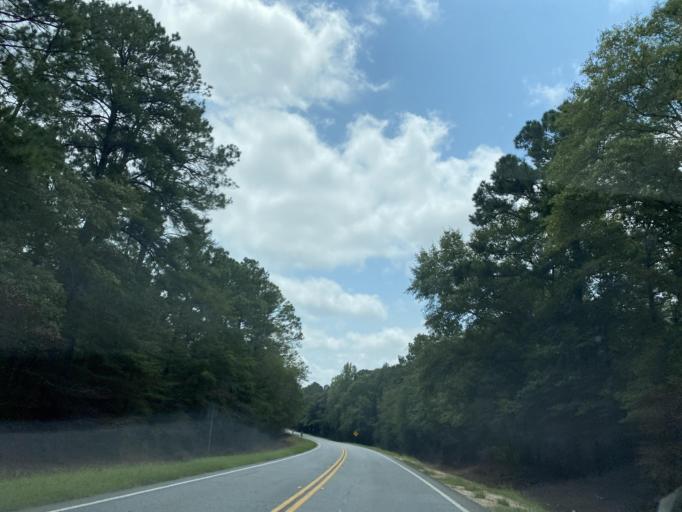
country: US
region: Georgia
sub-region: Wheeler County
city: Alamo
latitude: 32.1391
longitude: -82.7840
